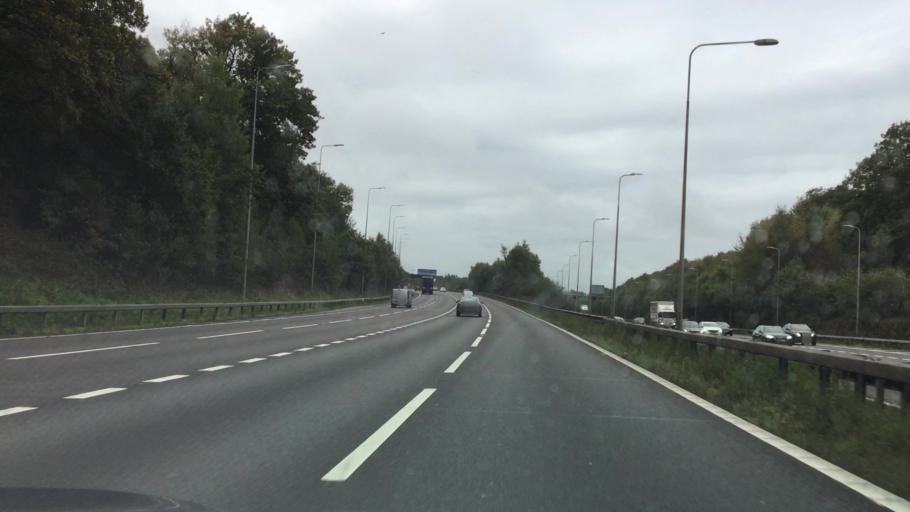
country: GB
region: England
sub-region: Solihull
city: Cheswick Green
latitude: 52.3557
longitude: -1.8082
